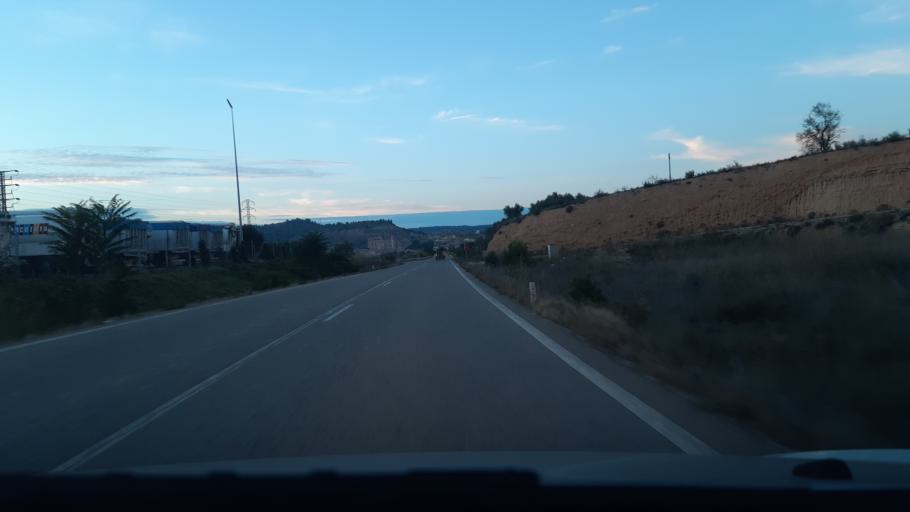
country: ES
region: Aragon
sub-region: Provincia de Teruel
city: Valderrobres
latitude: 40.8657
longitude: 0.1635
